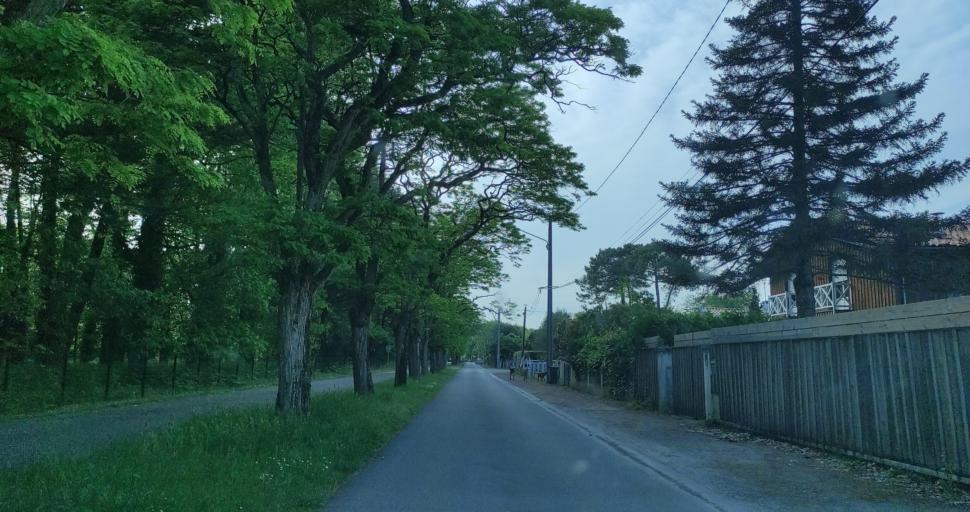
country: FR
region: Aquitaine
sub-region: Departement de la Gironde
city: Ares
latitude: 44.7554
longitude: -1.1308
